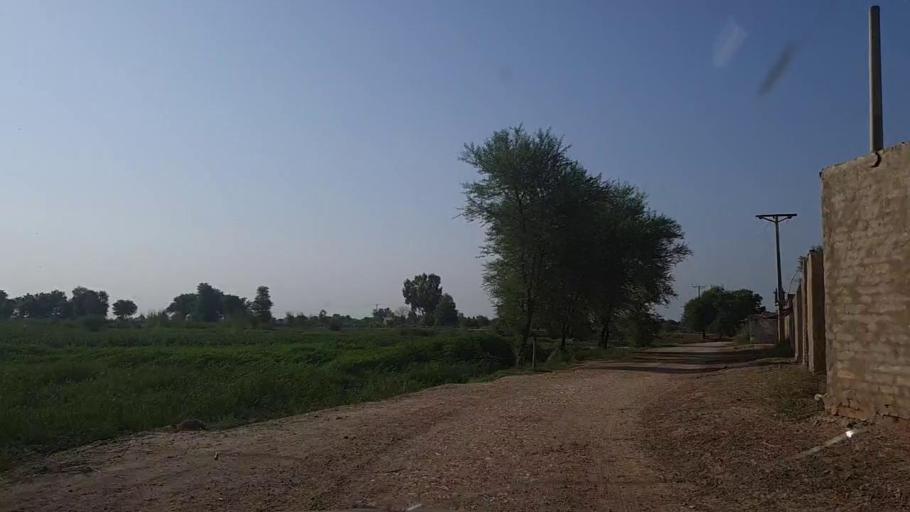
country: PK
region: Sindh
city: Khanpur
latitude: 27.7071
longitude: 69.3319
